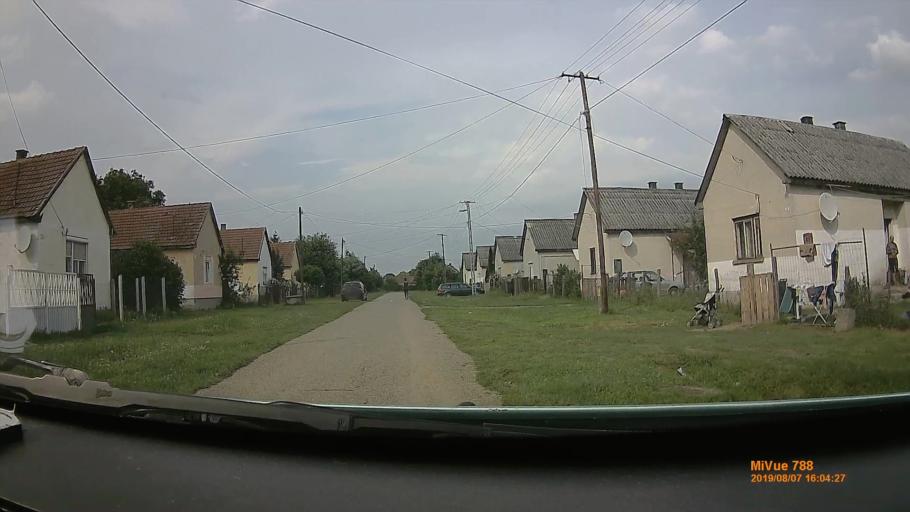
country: HU
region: Borsod-Abauj-Zemplen
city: Gonc
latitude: 48.5003
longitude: 21.2247
